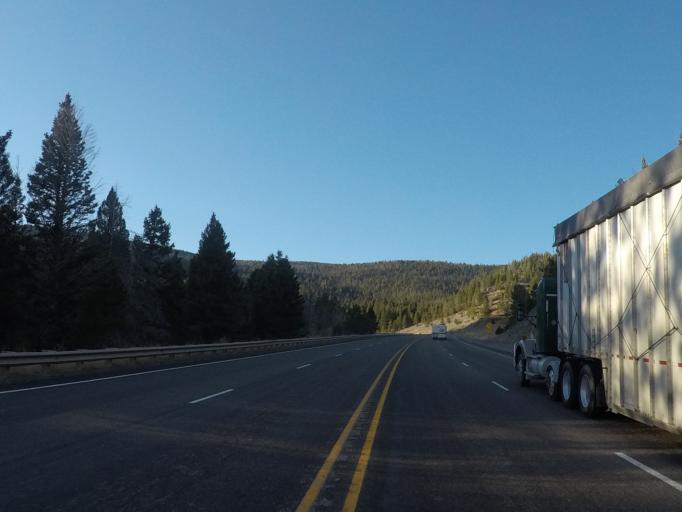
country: US
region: Montana
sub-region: Lewis and Clark County
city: Helena West Side
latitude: 46.5852
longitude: -112.2633
